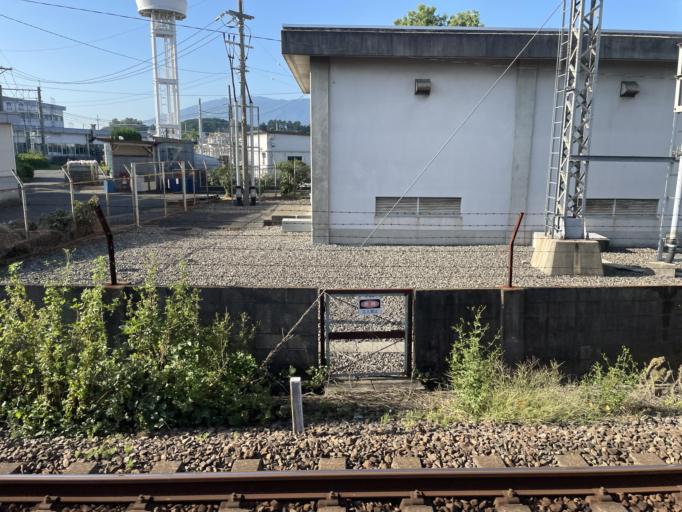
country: JP
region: Nara
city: Tawaramoto
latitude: 34.5398
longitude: 135.7098
